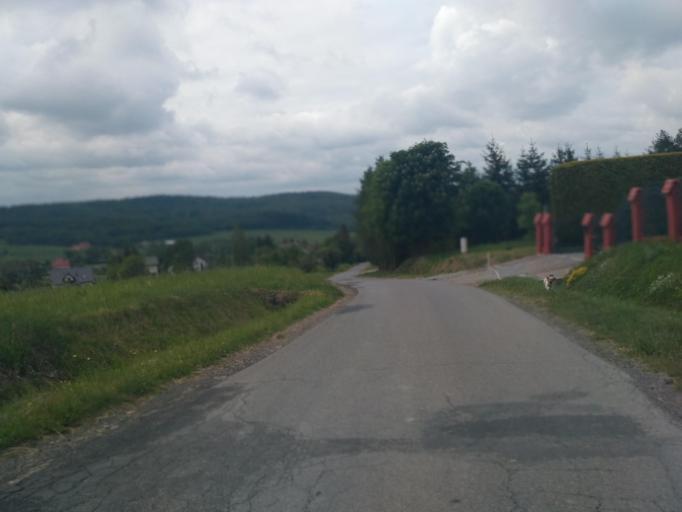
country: PL
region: Subcarpathian Voivodeship
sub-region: Powiat krosnienski
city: Chorkowka
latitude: 49.6677
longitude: 21.6401
